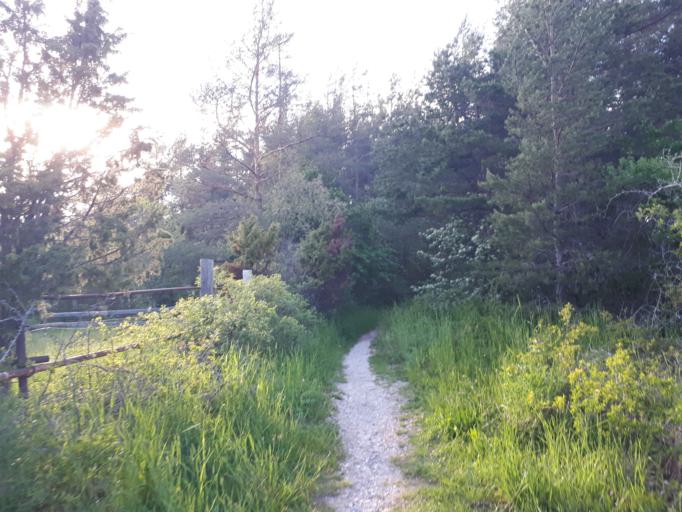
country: SE
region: Gotland
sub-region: Gotland
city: Visby
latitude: 57.6018
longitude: 18.3016
